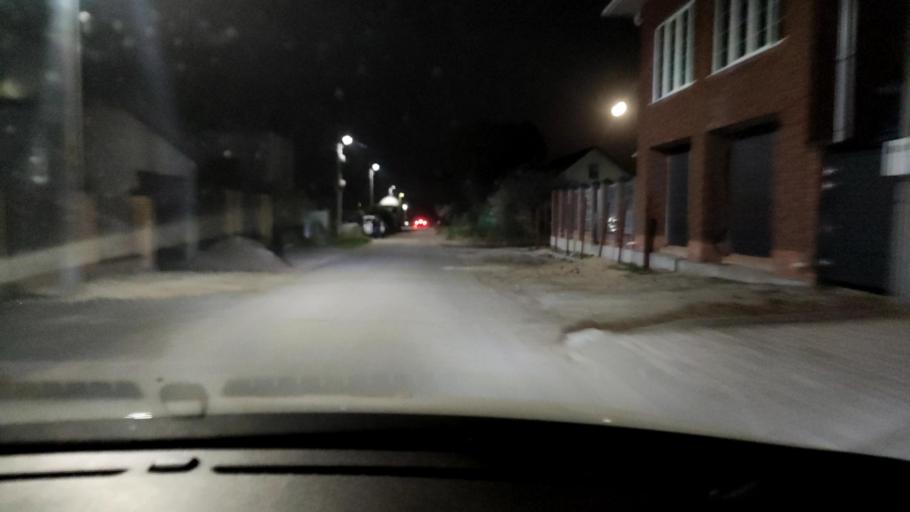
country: RU
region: Tatarstan
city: Stolbishchi
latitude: 55.7037
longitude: 49.1506
